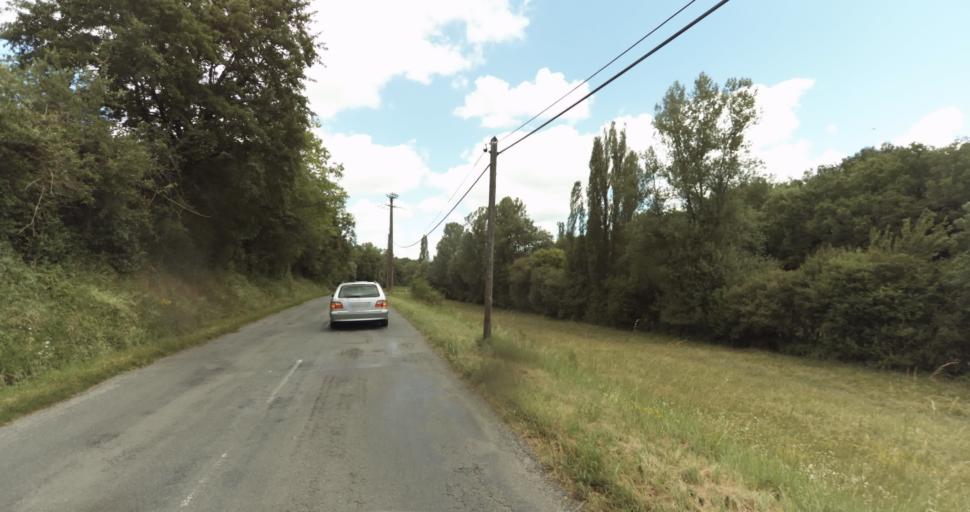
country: FR
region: Aquitaine
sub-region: Departement de la Dordogne
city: Beaumont-du-Perigord
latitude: 44.7523
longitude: 0.7608
